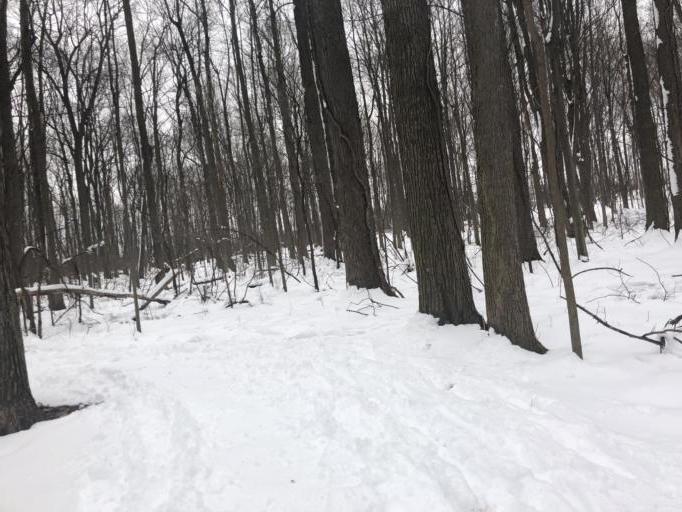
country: US
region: New York
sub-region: Monroe County
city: Pittsford
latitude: 43.0658
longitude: -77.5724
